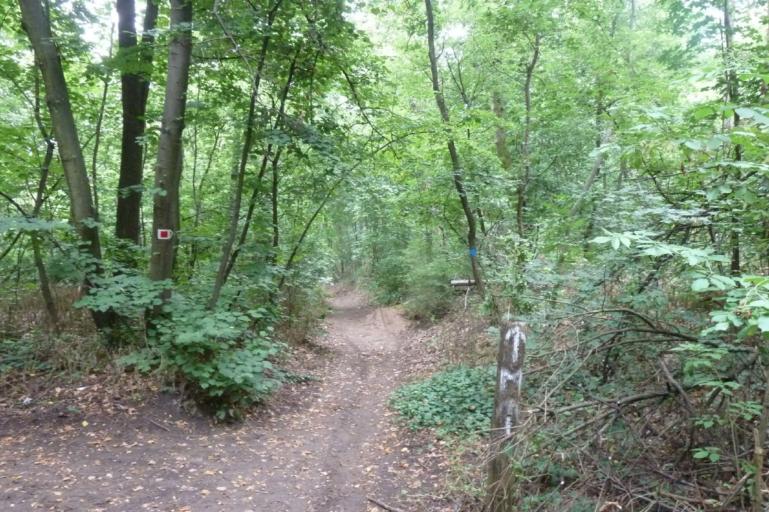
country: HU
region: Pest
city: Szada
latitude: 47.6269
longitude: 19.3461
